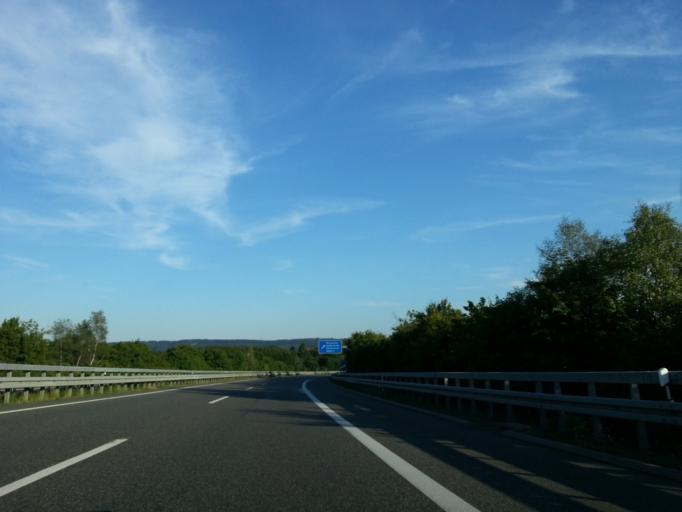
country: DE
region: Saarland
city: Nonnweiler
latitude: 49.6125
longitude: 6.9576
